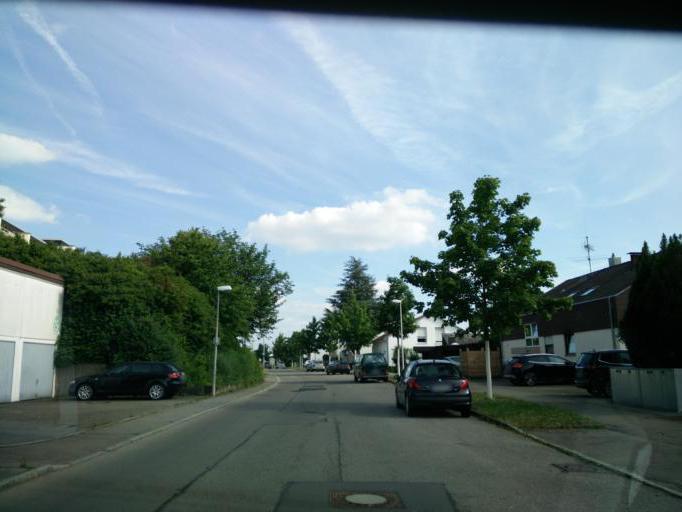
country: DE
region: Baden-Wuerttemberg
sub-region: Tuebingen Region
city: Tuebingen
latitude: 48.5389
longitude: 9.0492
